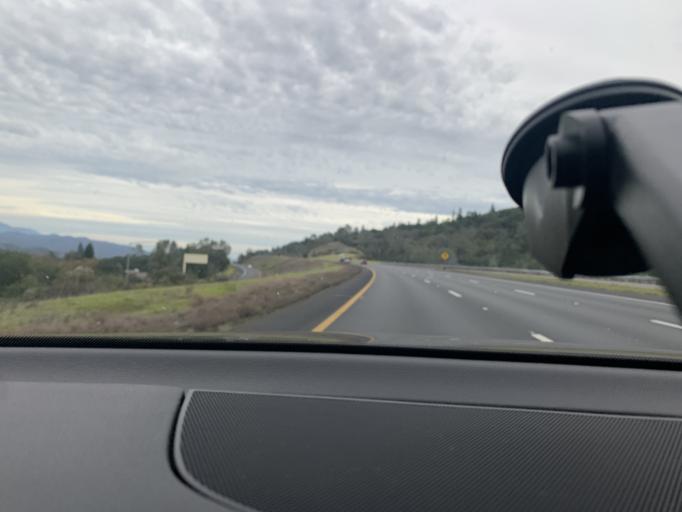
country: US
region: California
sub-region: Sonoma County
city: Healdsburg
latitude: 38.7108
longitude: -122.9169
